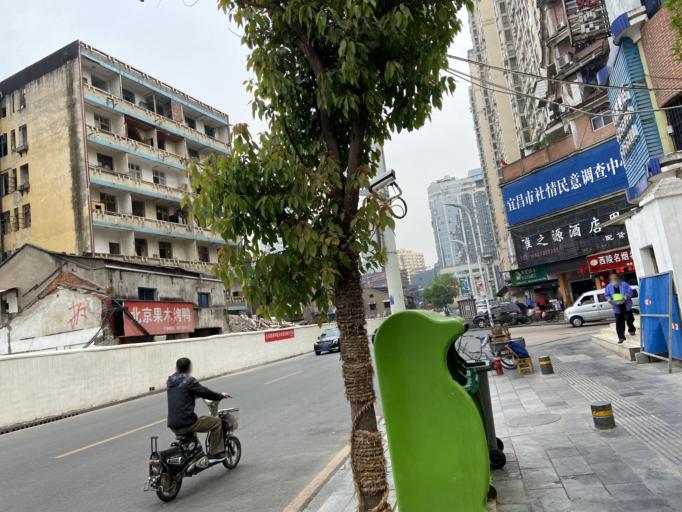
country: CN
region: Hubei
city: Dianjun
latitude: 30.6984
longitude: 111.2770
